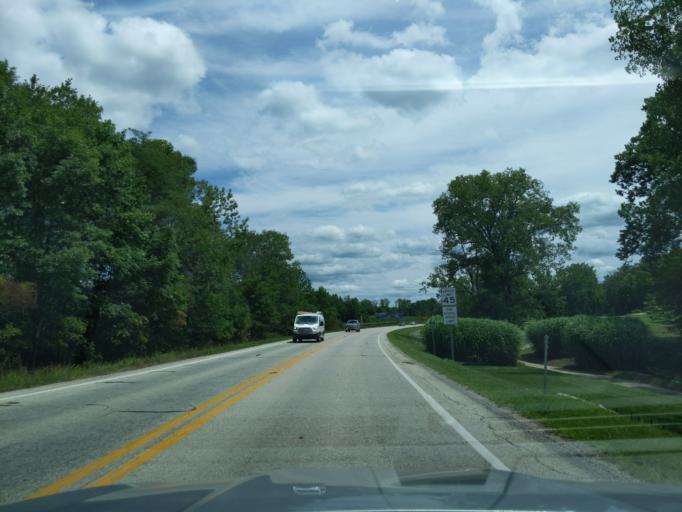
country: US
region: Indiana
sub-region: Ripley County
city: Batesville
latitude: 39.3100
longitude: -85.2302
